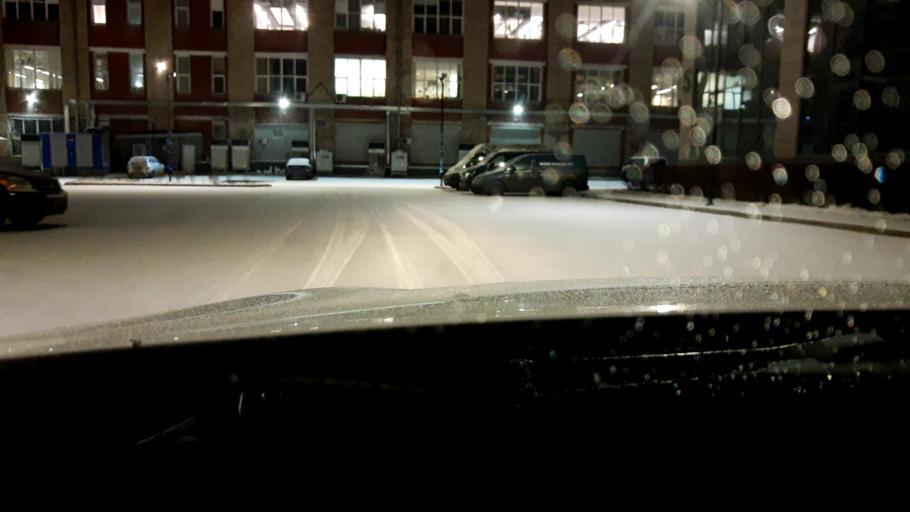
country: RU
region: Moscow
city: Mar'ina Roshcha
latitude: 55.7989
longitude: 37.6053
